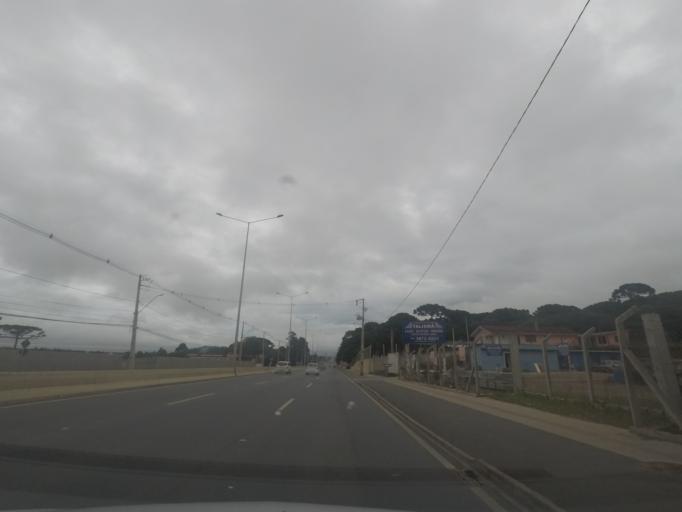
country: BR
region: Parana
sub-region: Piraquara
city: Piraquara
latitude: -25.4556
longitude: -49.1084
